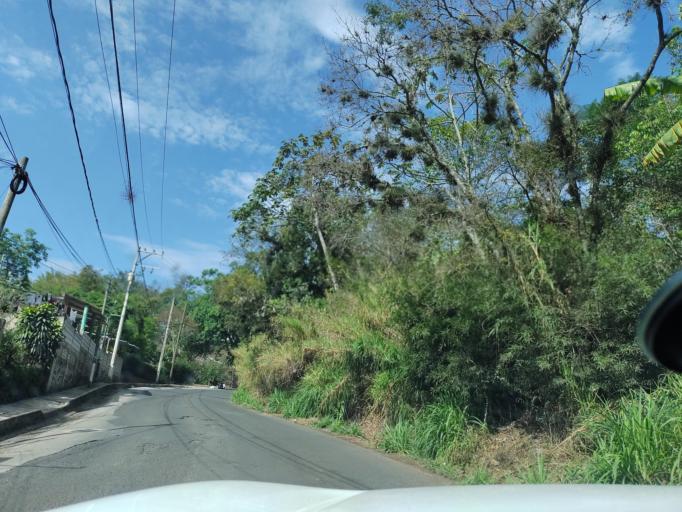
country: MX
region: Veracruz
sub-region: Coatepec
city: Las Lomas
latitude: 19.4833
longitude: -96.9291
